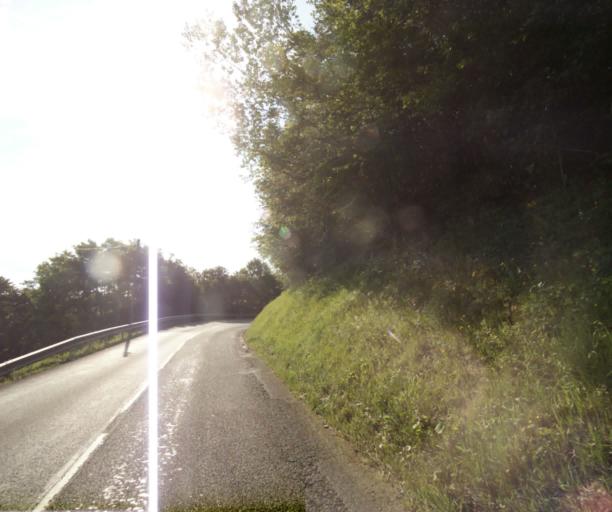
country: FR
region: Rhone-Alpes
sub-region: Departement de la Haute-Savoie
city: Armoy
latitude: 46.3597
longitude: 6.5148
